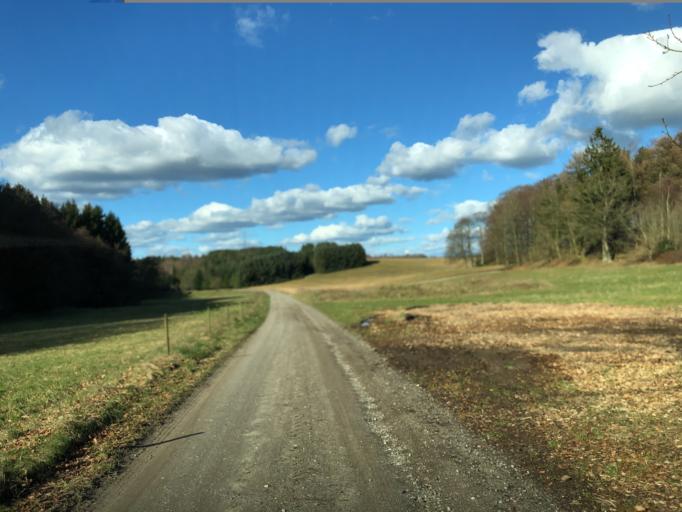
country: DK
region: Central Jutland
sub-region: Favrskov Kommune
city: Hammel
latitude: 56.3079
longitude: 9.9162
